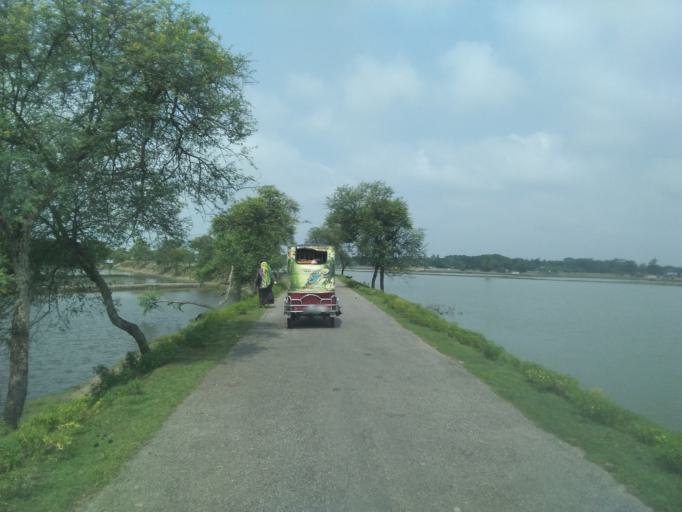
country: BD
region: Khulna
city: Phultala
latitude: 22.7052
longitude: 89.4606
